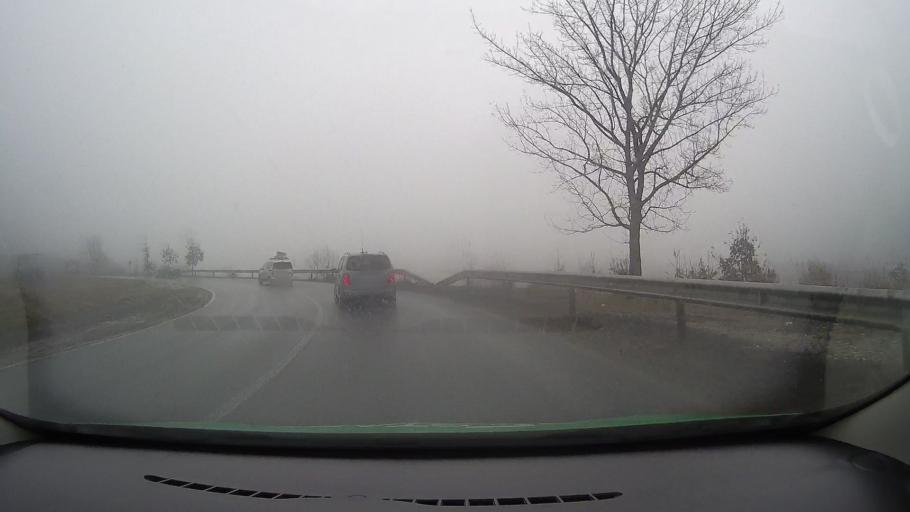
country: RO
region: Timis
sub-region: Comuna Curtea
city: Curtea
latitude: 45.8472
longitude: 22.3227
